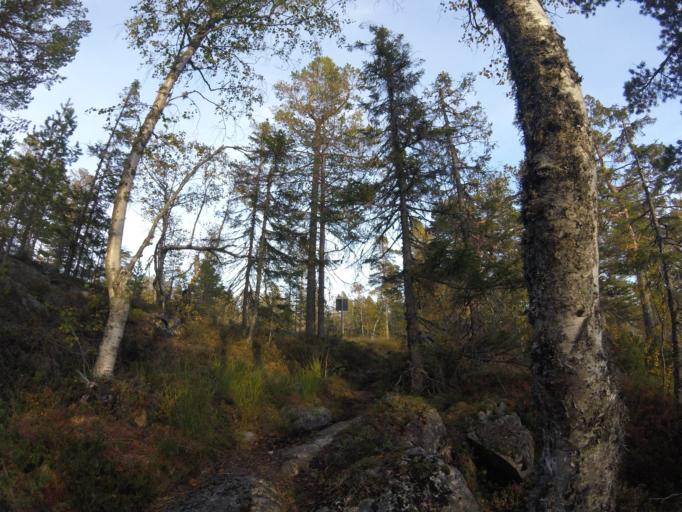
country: NO
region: Buskerud
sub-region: Flesberg
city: Lampeland
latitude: 59.6838
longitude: 9.4505
